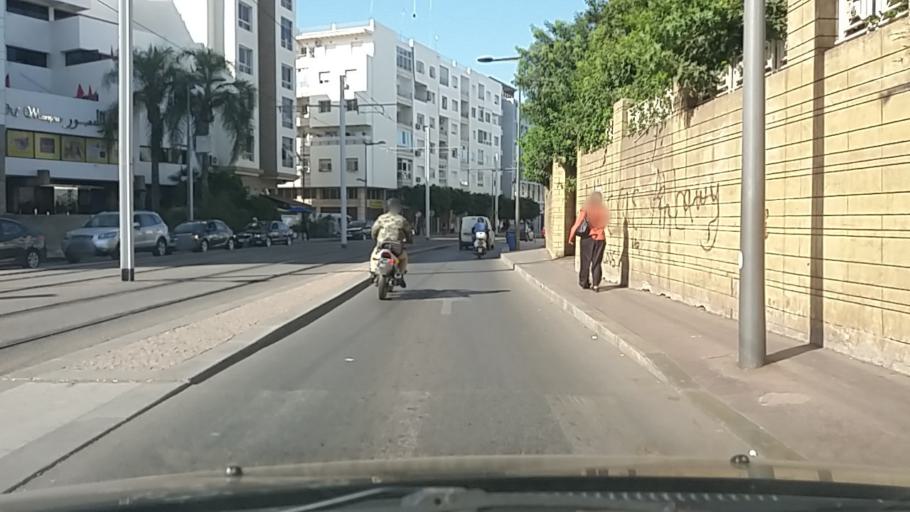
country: MA
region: Rabat-Sale-Zemmour-Zaer
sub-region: Rabat
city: Rabat
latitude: 34.0181
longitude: -6.8284
